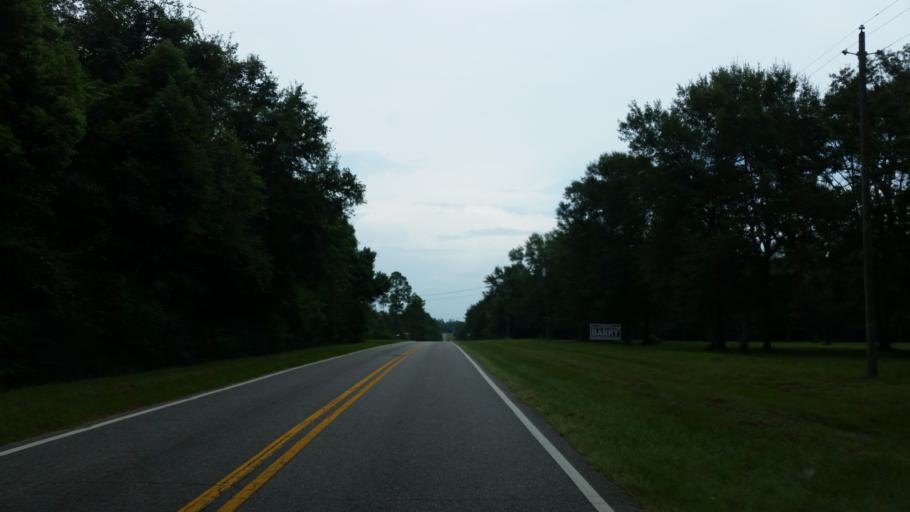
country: US
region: Florida
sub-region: Escambia County
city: Molino
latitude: 30.6799
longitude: -87.3315
